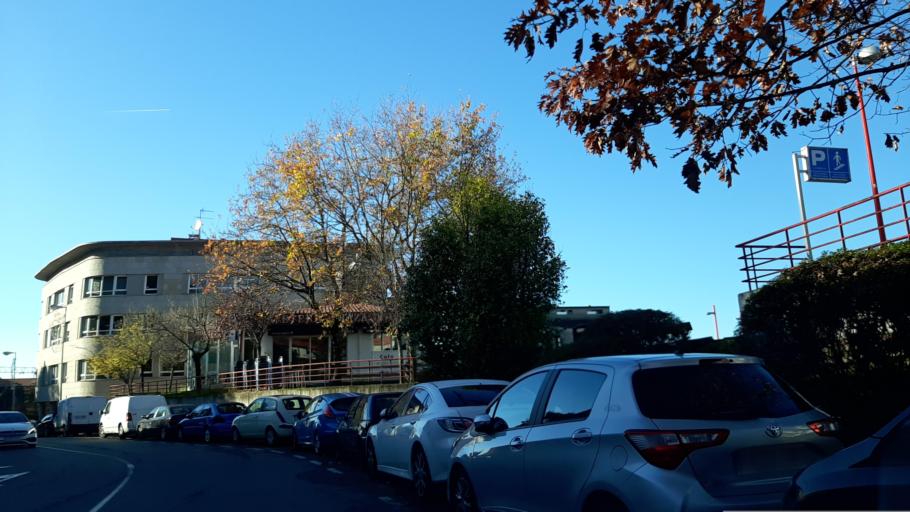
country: ES
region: Galicia
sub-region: Provincia de Pontevedra
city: Vigo
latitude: 42.2352
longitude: -8.7265
